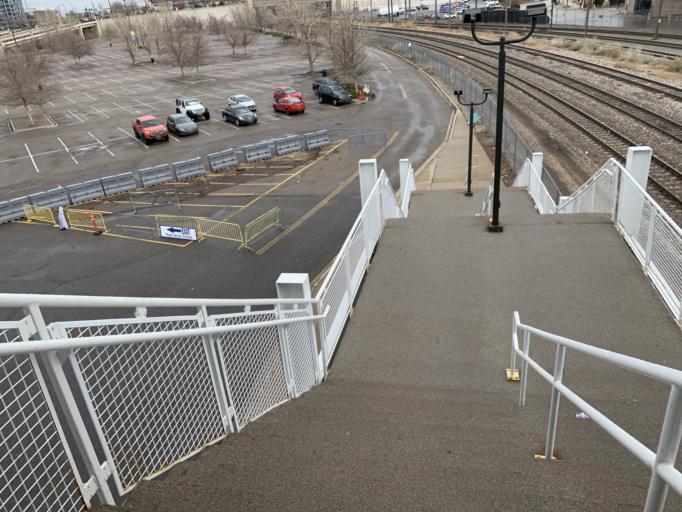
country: US
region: Colorado
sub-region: Denver County
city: Denver
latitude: 39.7491
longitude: -105.0093
